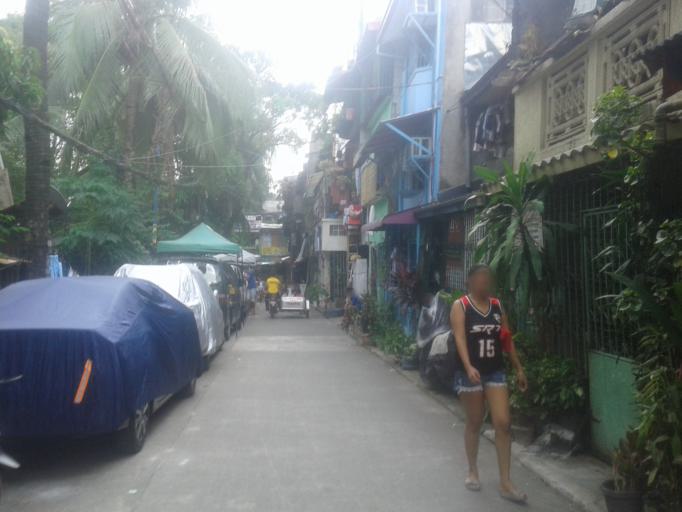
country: PH
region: Metro Manila
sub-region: Mandaluyong
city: Mandaluyong City
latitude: 14.5845
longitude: 121.0403
